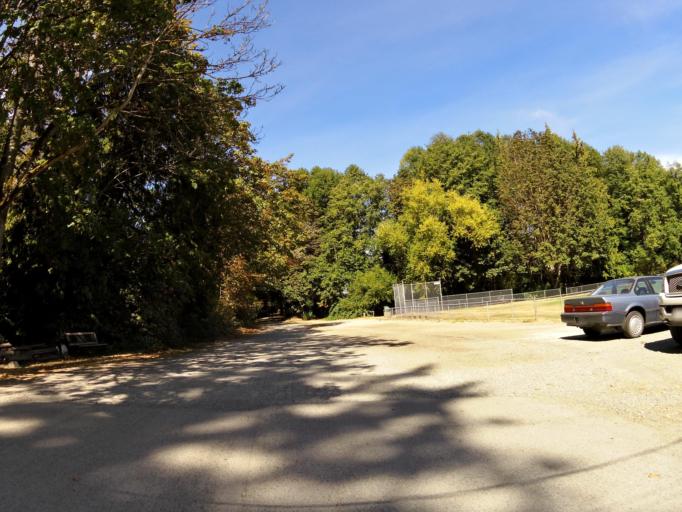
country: CA
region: British Columbia
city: Victoria
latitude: 48.5345
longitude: -123.3771
